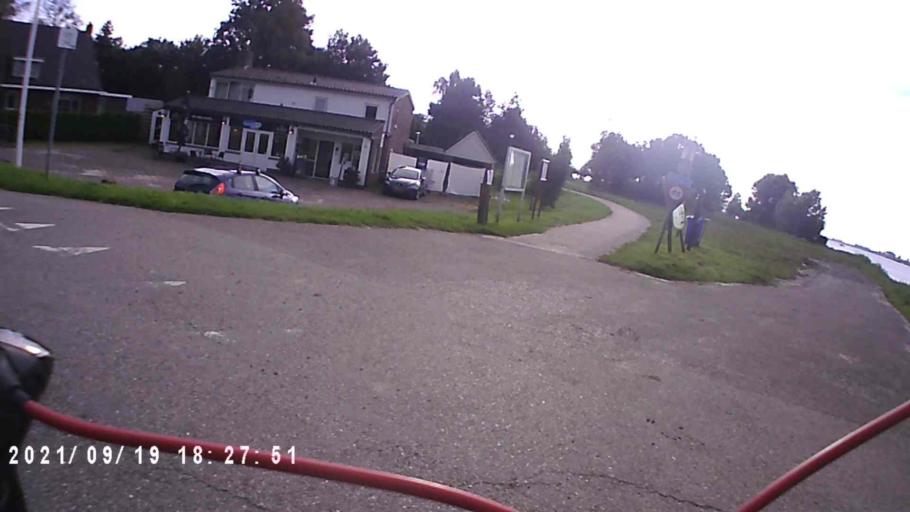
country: NL
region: Groningen
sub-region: Gemeente Appingedam
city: Appingedam
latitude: 53.2734
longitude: 6.8431
